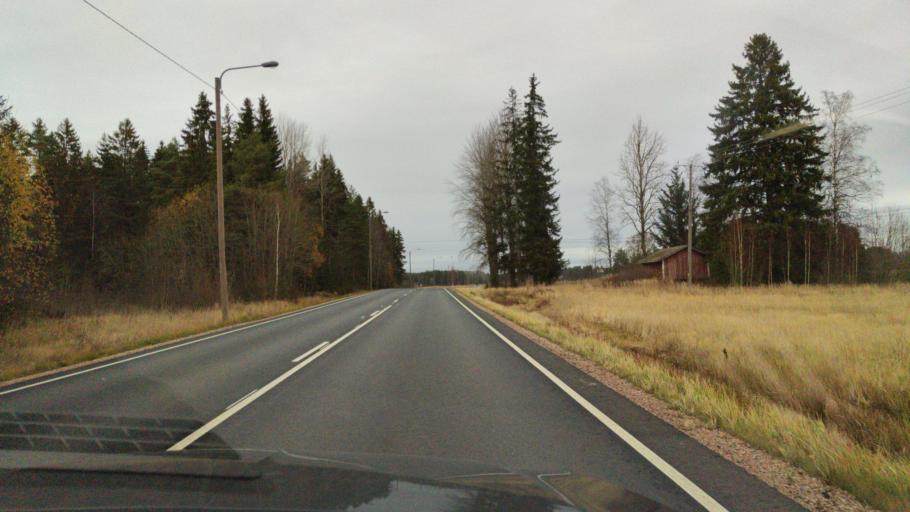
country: FI
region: Varsinais-Suomi
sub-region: Turku
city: Vahto
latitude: 60.6684
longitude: 22.4351
